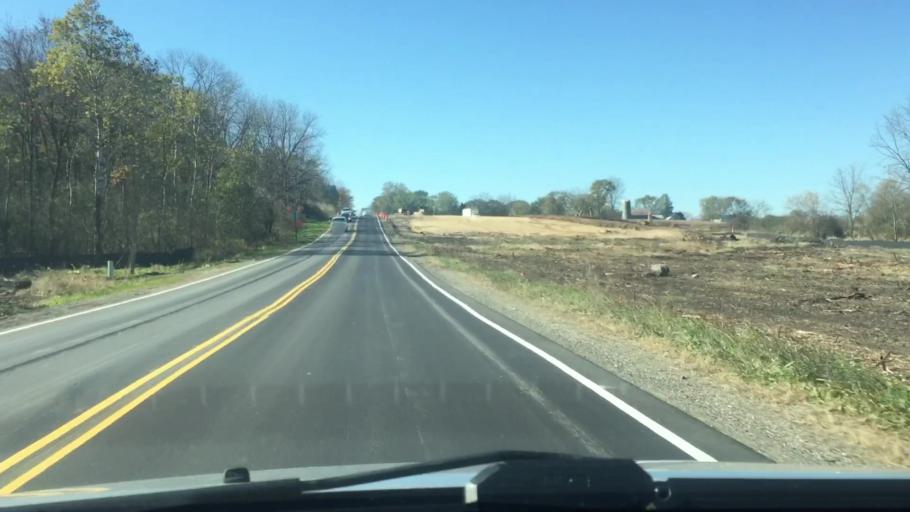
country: US
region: Wisconsin
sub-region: Waukesha County
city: Waukesha
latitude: 42.9886
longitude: -88.2820
